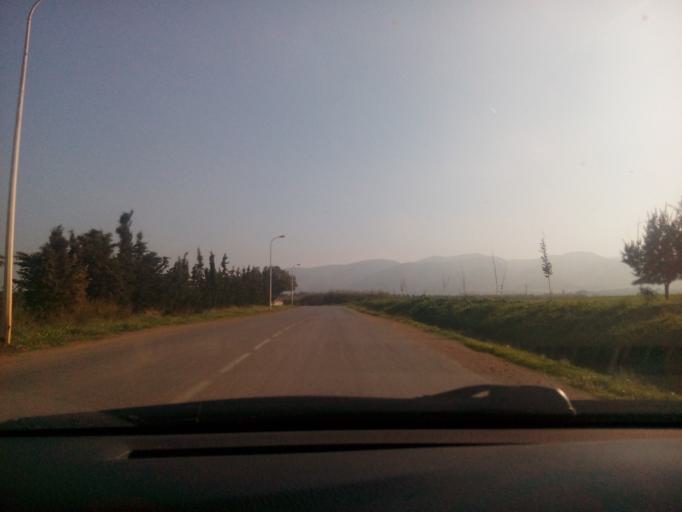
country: DZ
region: Oran
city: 'Ain el Turk
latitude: 35.6999
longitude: -0.8815
